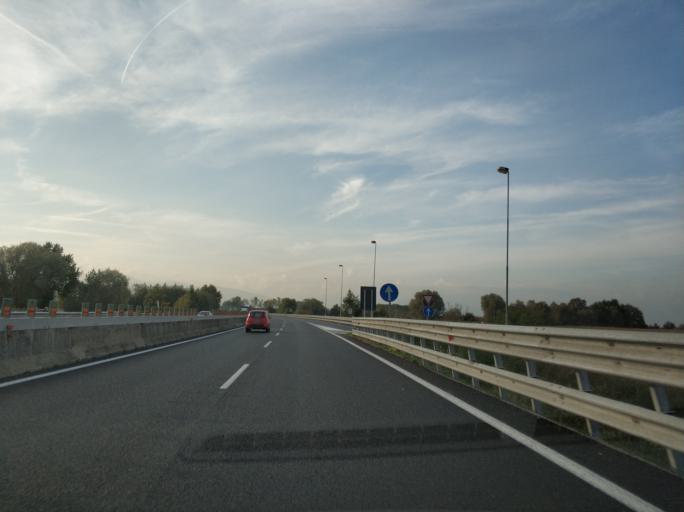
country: IT
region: Piedmont
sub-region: Provincia di Torino
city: Borgaro Torinese
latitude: 45.1719
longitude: 7.6764
